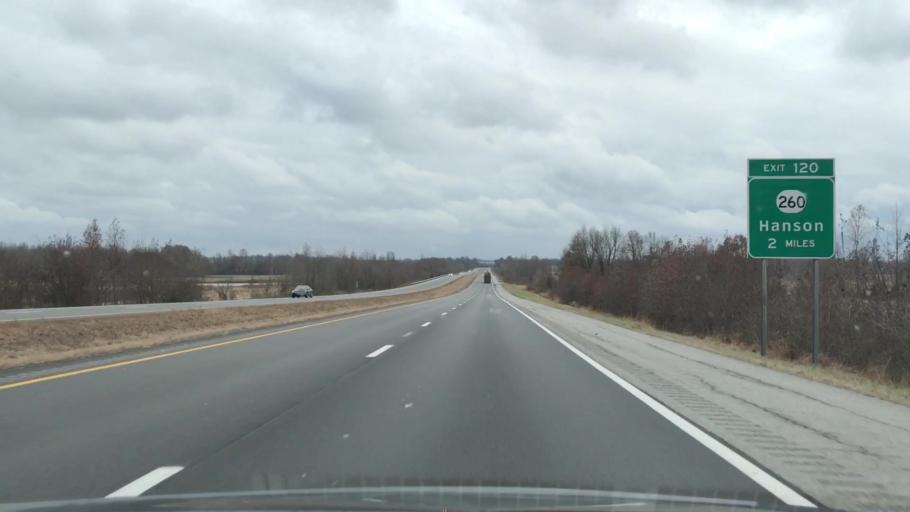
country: US
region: Kentucky
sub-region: Hopkins County
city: Madisonville
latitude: 37.4497
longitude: -87.4774
